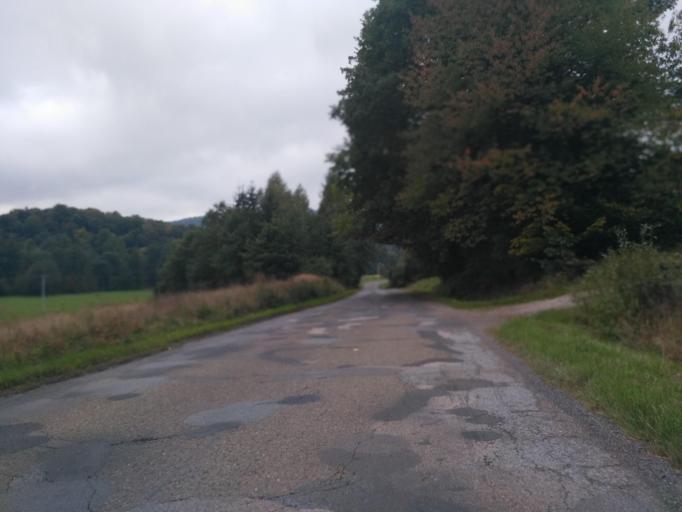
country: PL
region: Subcarpathian Voivodeship
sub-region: Powiat debicki
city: Brzostek
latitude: 49.9238
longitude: 21.4602
